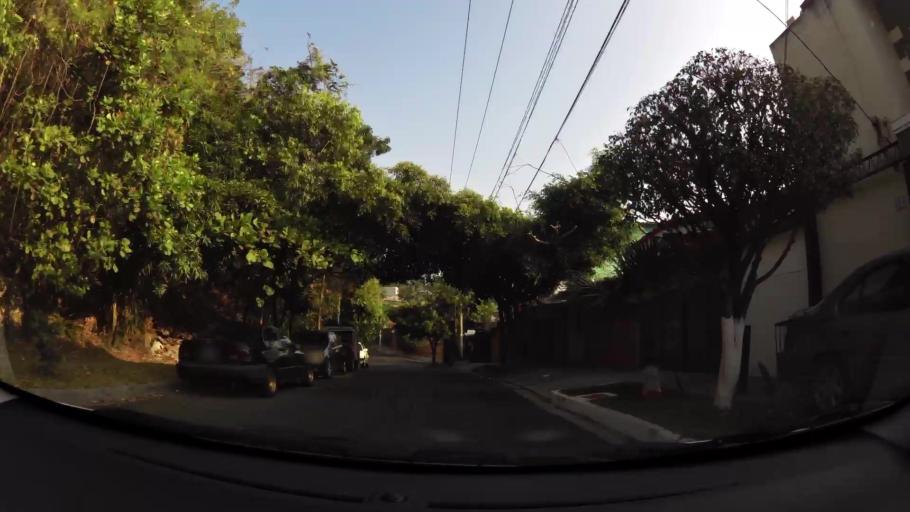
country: SV
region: San Salvador
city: San Salvador
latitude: 13.6820
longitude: -89.2028
